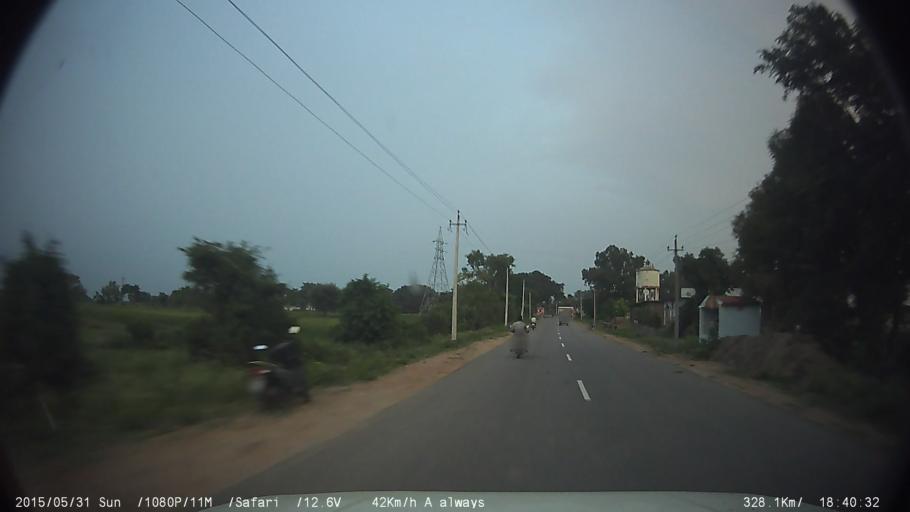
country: IN
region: Karnataka
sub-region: Mysore
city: Nanjangud
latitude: 12.1485
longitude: 76.7866
